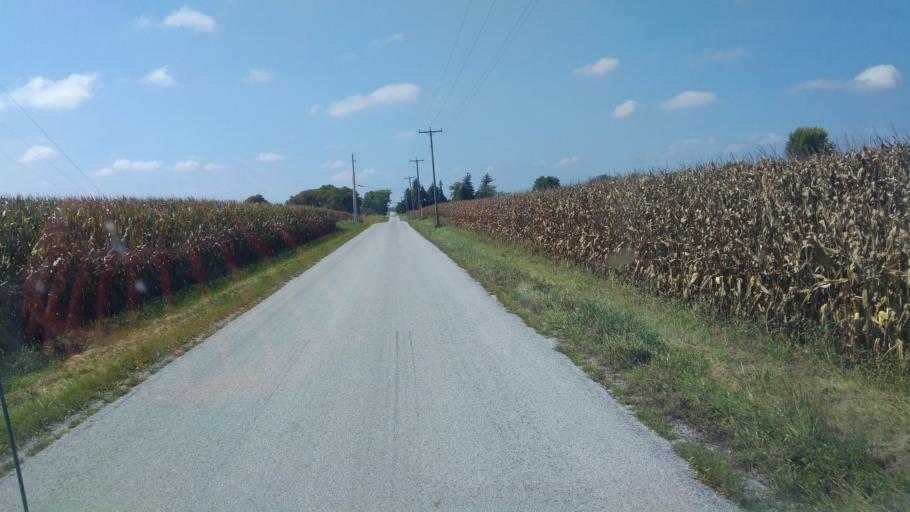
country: US
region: Ohio
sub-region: Hardin County
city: Kenton
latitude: 40.6745
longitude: -83.6068
